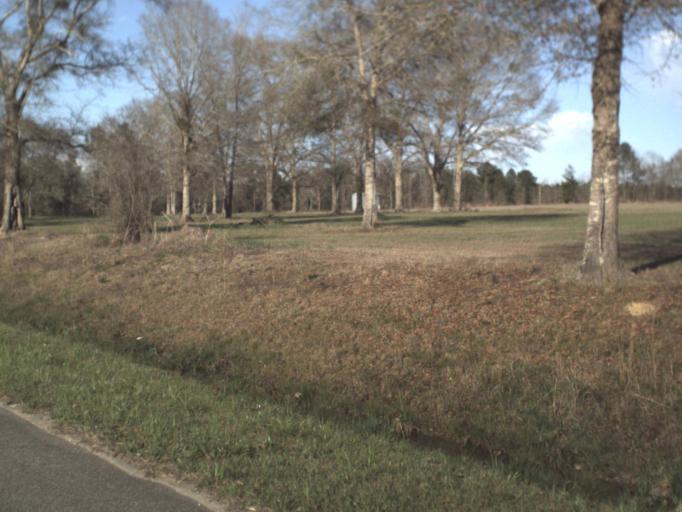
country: US
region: Florida
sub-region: Jackson County
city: Marianna
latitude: 30.7185
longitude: -85.2306
